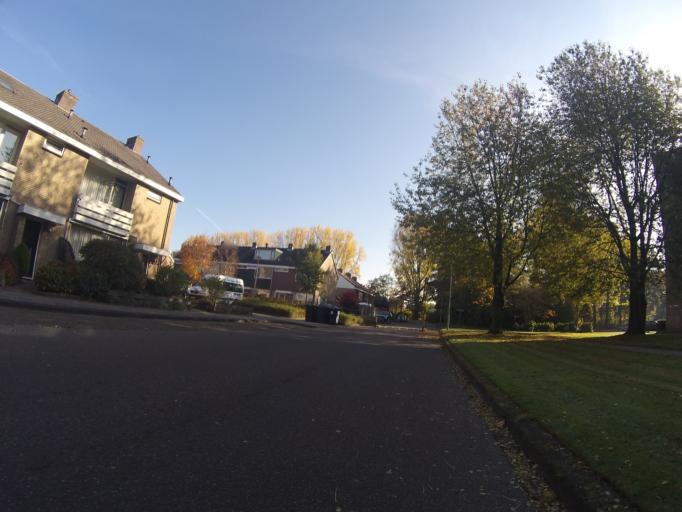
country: NL
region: Gelderland
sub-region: Gemeente Nijkerk
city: Nijkerk
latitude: 52.2159
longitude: 5.4822
